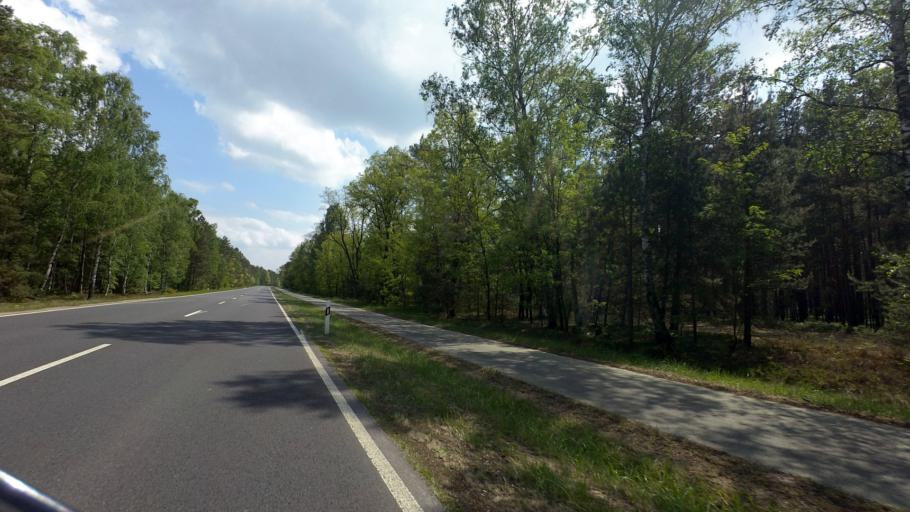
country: DE
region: Saxony
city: Rietschen
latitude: 51.4482
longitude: 14.7705
